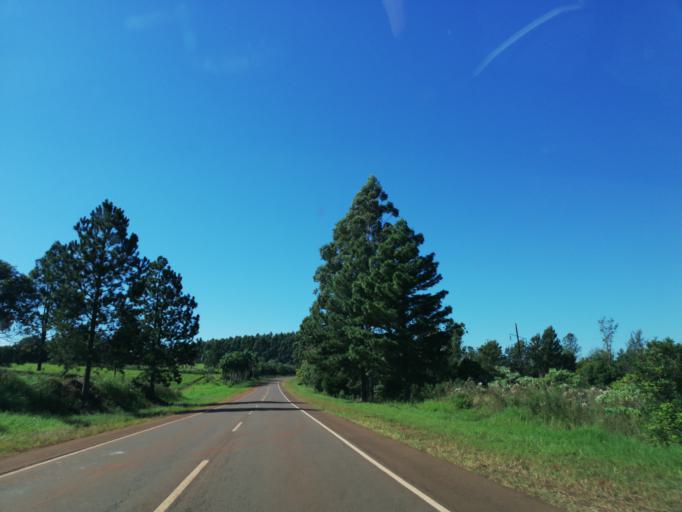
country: AR
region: Misiones
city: Dos de Mayo
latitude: -27.0696
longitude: -54.4118
